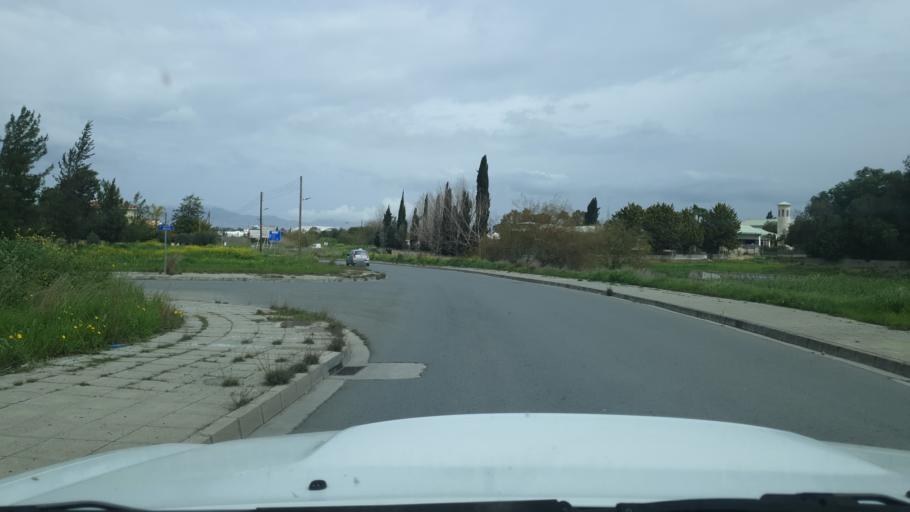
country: CY
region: Lefkosia
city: Tseri
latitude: 35.1038
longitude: 33.3556
